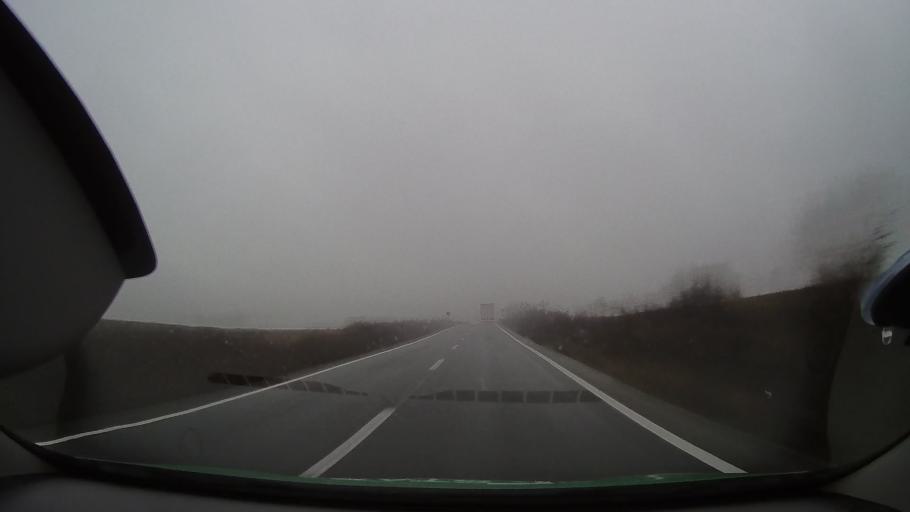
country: RO
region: Bihor
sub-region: Comuna Olcea
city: Olcea
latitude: 46.6773
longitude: 21.9656
